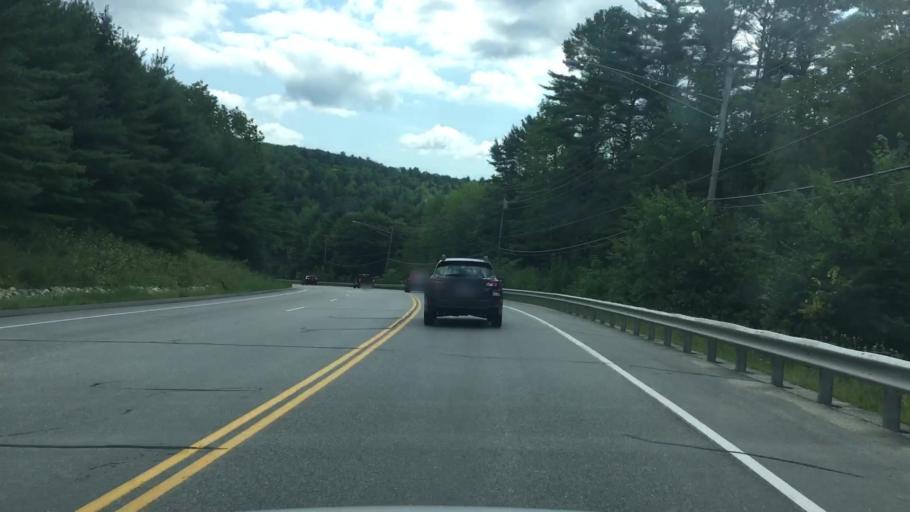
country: US
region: Maine
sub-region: Kennebec County
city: Augusta
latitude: 44.3331
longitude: -69.7928
